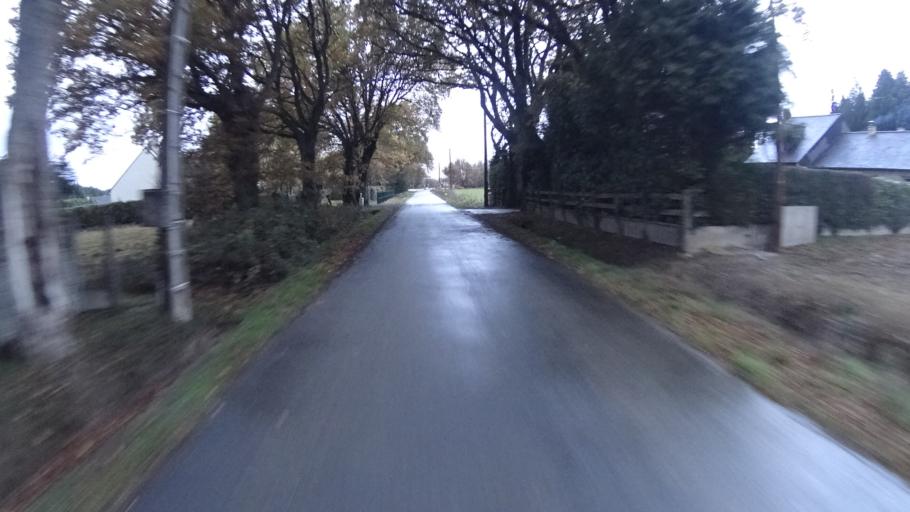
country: FR
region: Brittany
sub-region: Departement d'Ille-et-Vilaine
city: Bains-sur-Oust
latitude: 47.6863
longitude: -2.0507
